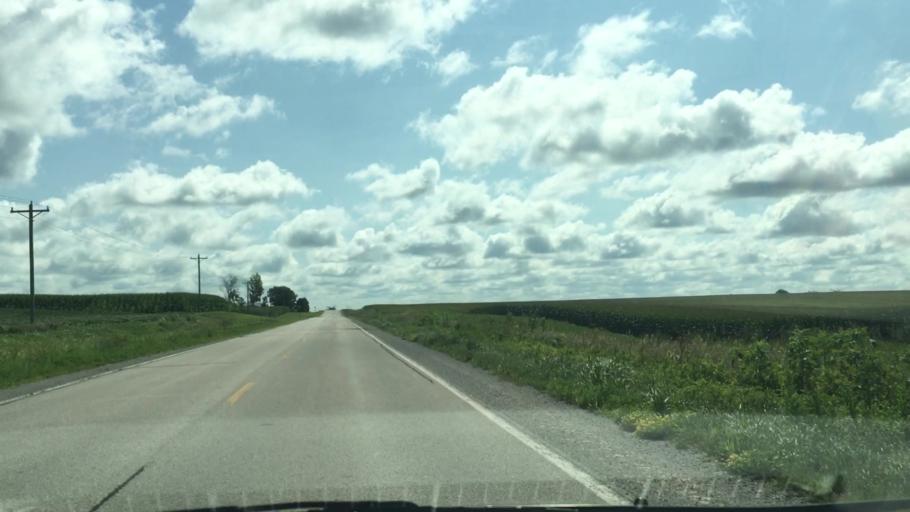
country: US
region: Iowa
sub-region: Johnson County
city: Solon
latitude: 41.8310
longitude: -91.4508
